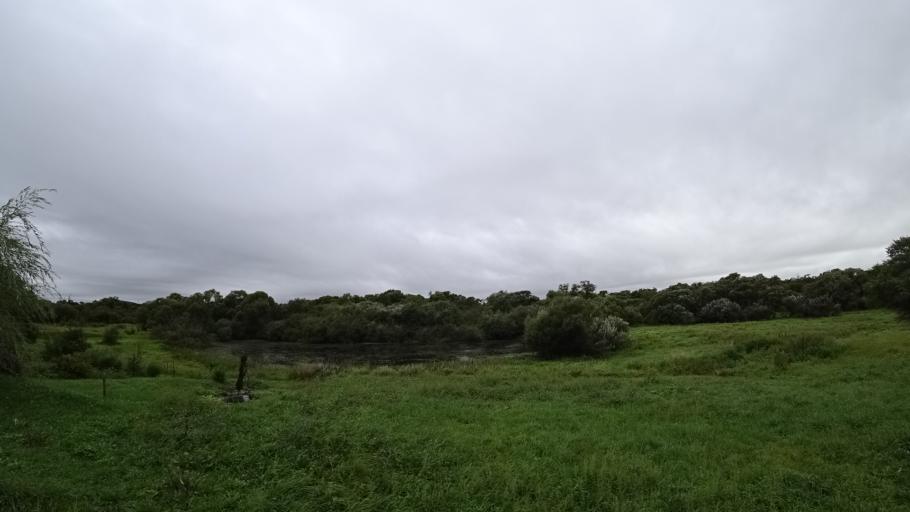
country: RU
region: Primorskiy
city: Monastyrishche
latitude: 44.2709
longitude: 132.4046
